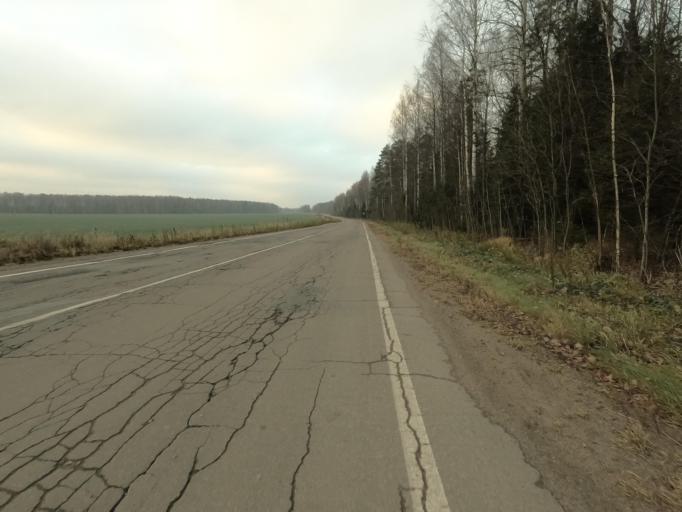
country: RU
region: Leningrad
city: Mga
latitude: 59.7959
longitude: 31.0041
